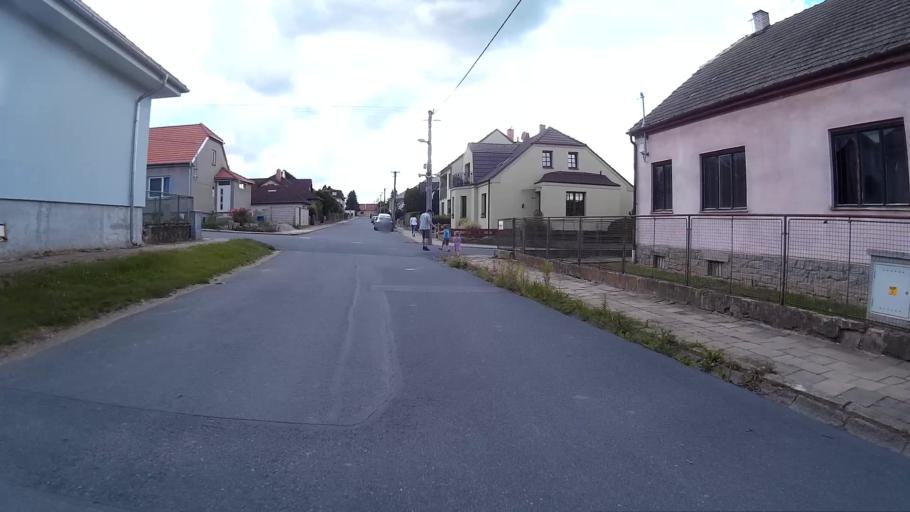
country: CZ
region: South Moravian
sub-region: Okres Brno-Venkov
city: Rosice
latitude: 49.1847
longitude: 16.3961
